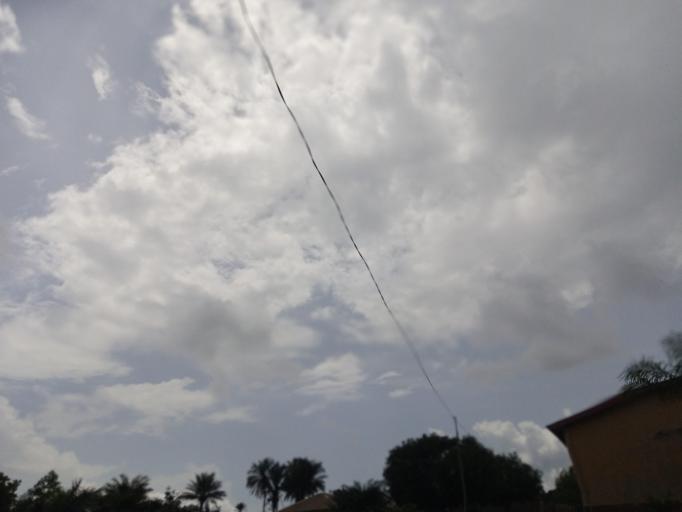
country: SL
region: Northern Province
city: Sawkta
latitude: 8.6352
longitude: -13.2016
